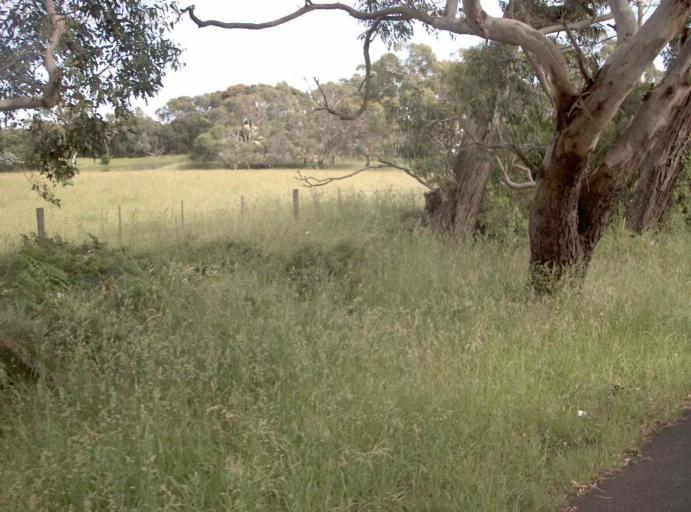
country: AU
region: Victoria
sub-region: Bass Coast
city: Phillip Island
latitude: -38.4696
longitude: 145.2390
